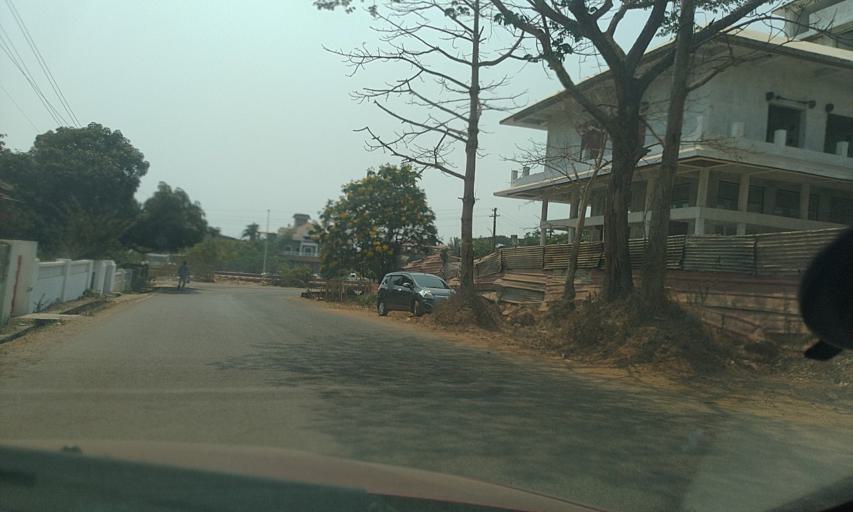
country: IN
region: Goa
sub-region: North Goa
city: Panaji
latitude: 15.5205
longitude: 73.8304
